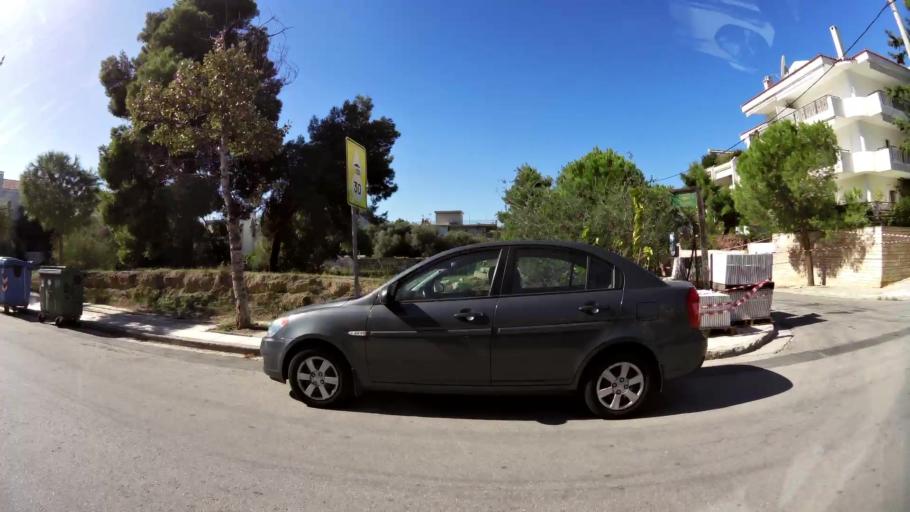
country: GR
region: Attica
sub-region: Nomarchia Anatolikis Attikis
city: Vouliagmeni
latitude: 37.8170
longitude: 23.7813
